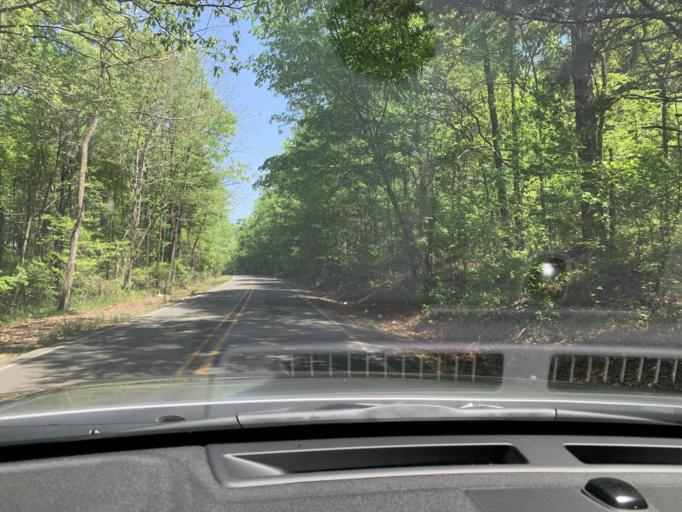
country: US
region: Georgia
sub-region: Polk County
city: Aragon
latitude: 34.0835
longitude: -85.1504
